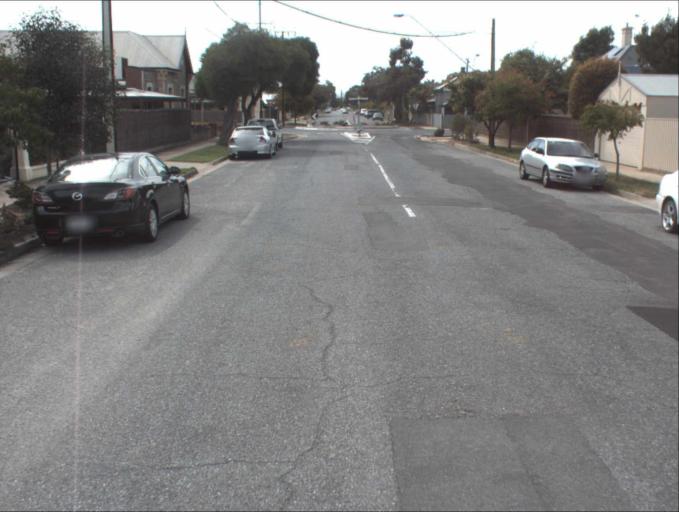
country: AU
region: South Australia
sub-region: Port Adelaide Enfield
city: Birkenhead
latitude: -34.8349
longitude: 138.4872
